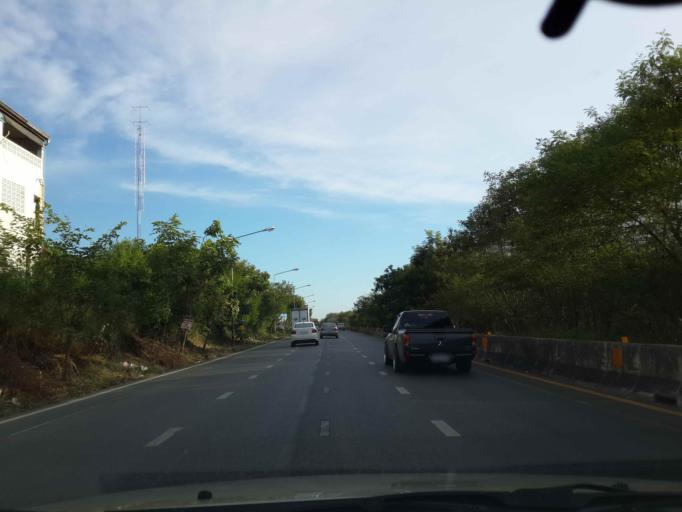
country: TH
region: Chon Buri
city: Phatthaya
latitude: 12.9307
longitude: 100.9051
